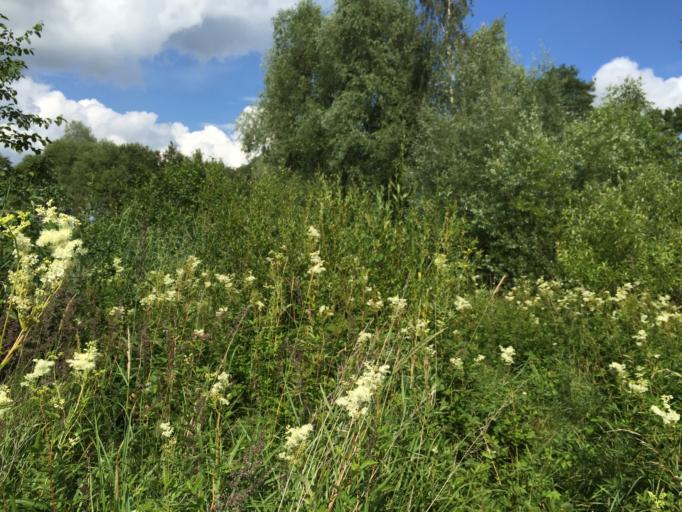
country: LV
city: Tervete
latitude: 56.6147
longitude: 23.4454
